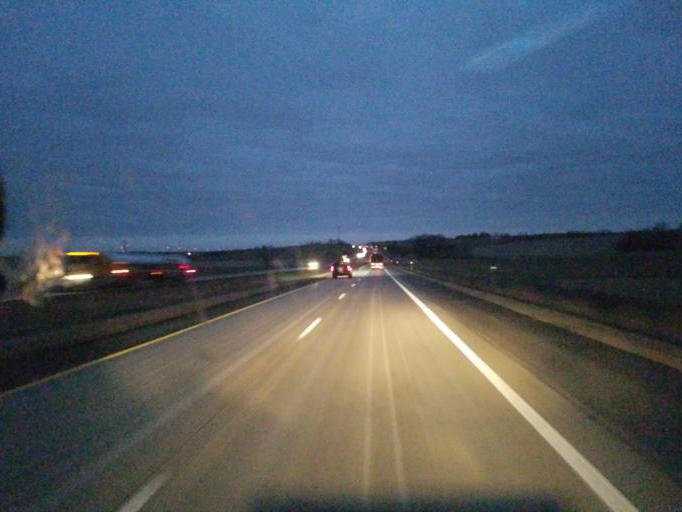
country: US
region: Iowa
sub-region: Cass County
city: Atlantic
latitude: 41.4965
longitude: -94.7982
